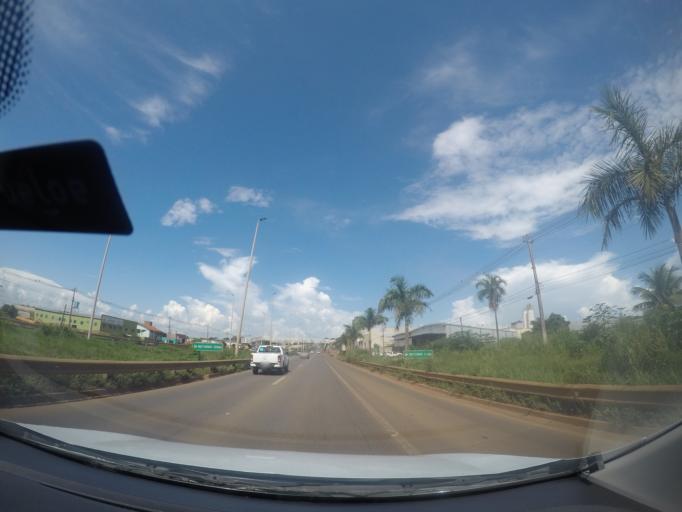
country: BR
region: Goias
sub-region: Goiania
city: Goiania
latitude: -16.6594
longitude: -49.3597
